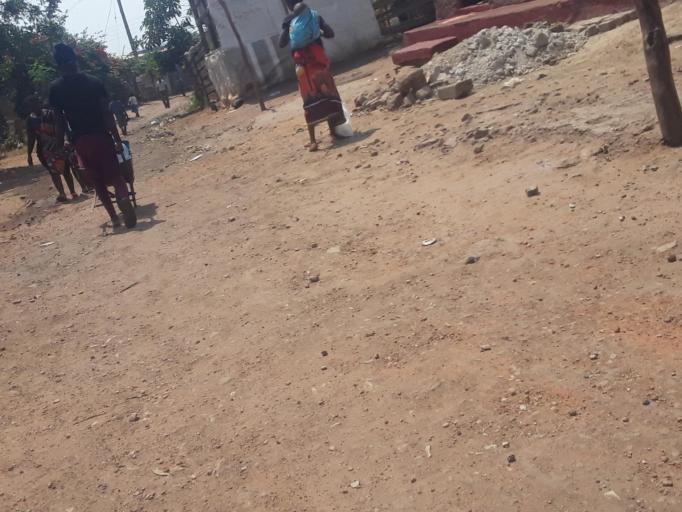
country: ZM
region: Lusaka
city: Lusaka
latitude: -15.3624
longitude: 28.2997
